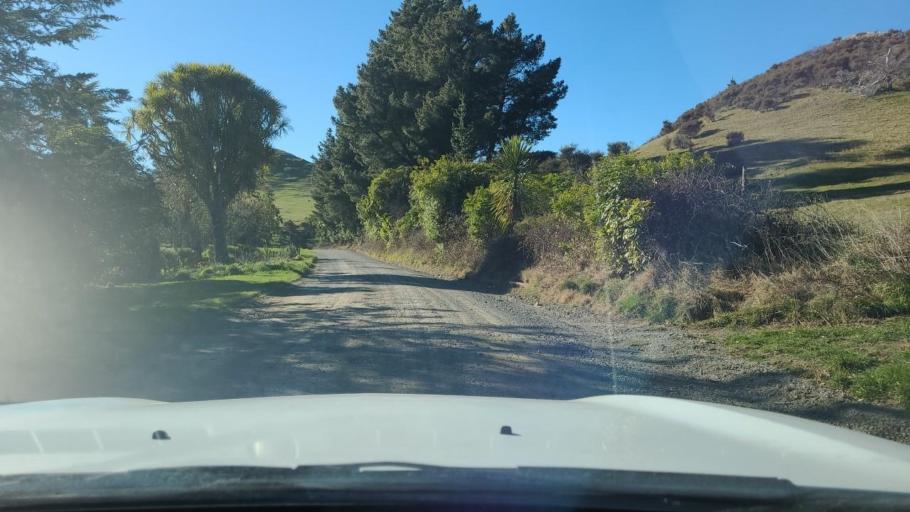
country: NZ
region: Hawke's Bay
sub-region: Napier City
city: Taradale
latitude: -39.3416
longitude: 176.5595
